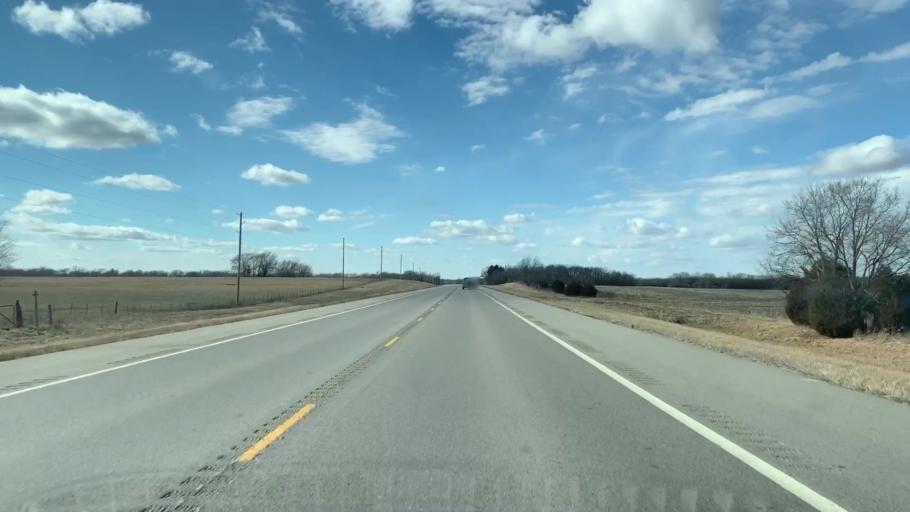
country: US
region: Kansas
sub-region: Labette County
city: Oswego
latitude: 37.3400
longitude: -95.0537
